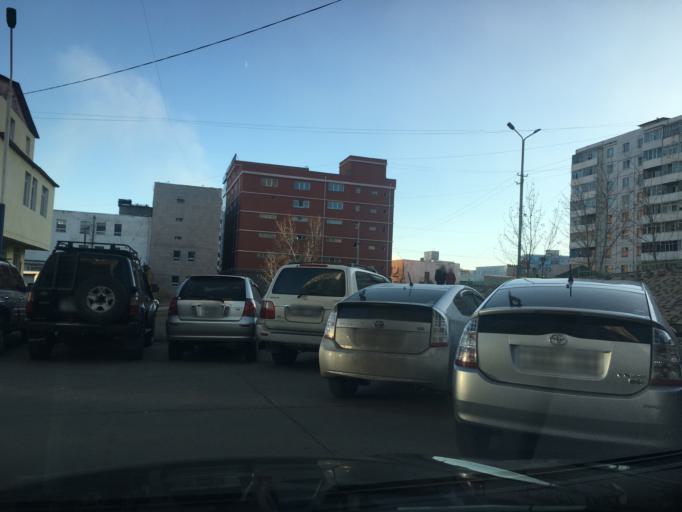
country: MN
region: Ulaanbaatar
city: Ulaanbaatar
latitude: 47.9244
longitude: 106.8825
